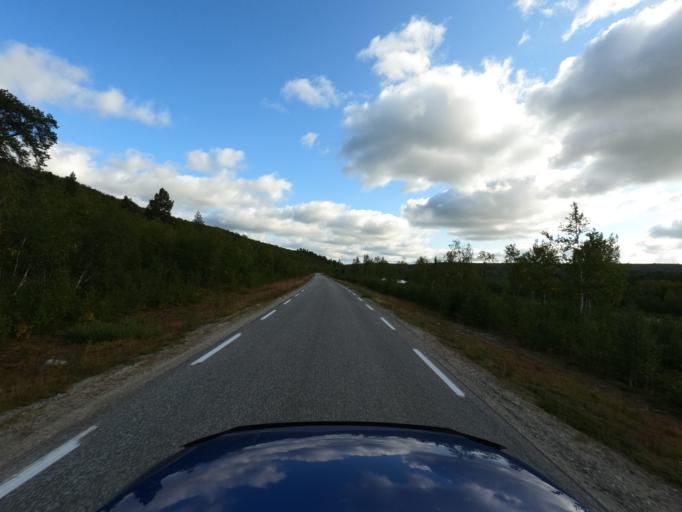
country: NO
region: Finnmark Fylke
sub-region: Porsanger
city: Lakselv
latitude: 69.4240
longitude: 24.8314
